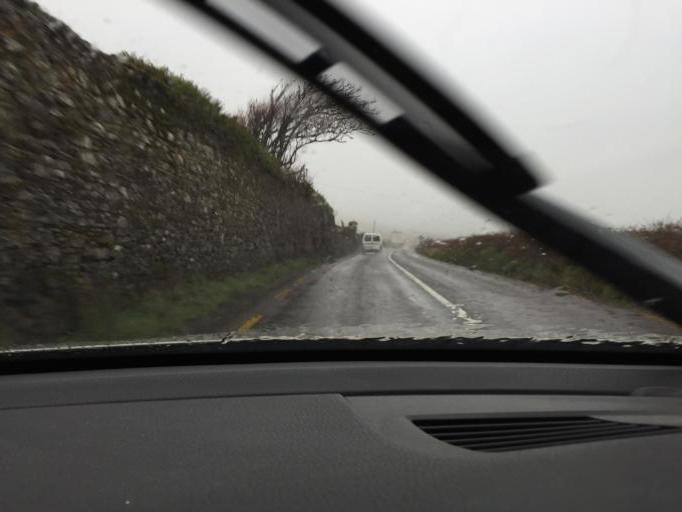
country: IE
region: Munster
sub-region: Ciarrai
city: Dingle
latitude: 52.1311
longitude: -10.2448
